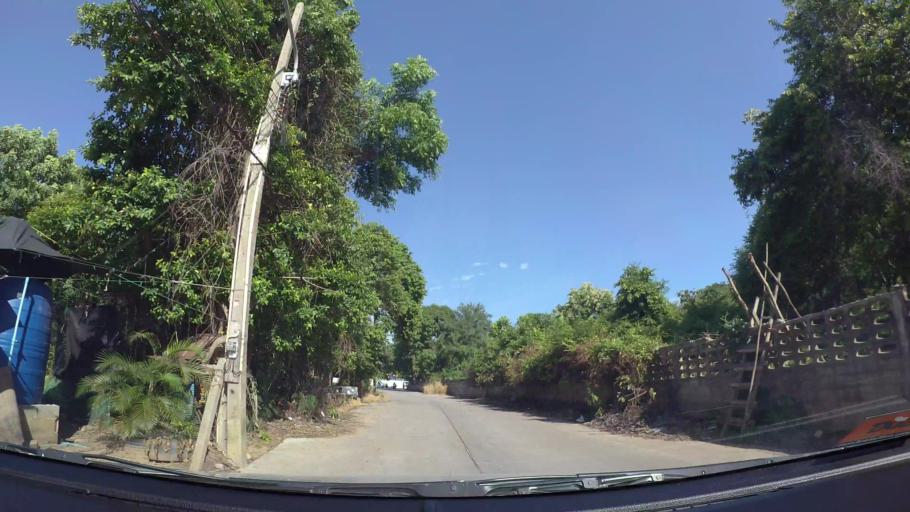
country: TH
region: Chon Buri
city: Si Racha
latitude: 13.1589
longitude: 100.9279
